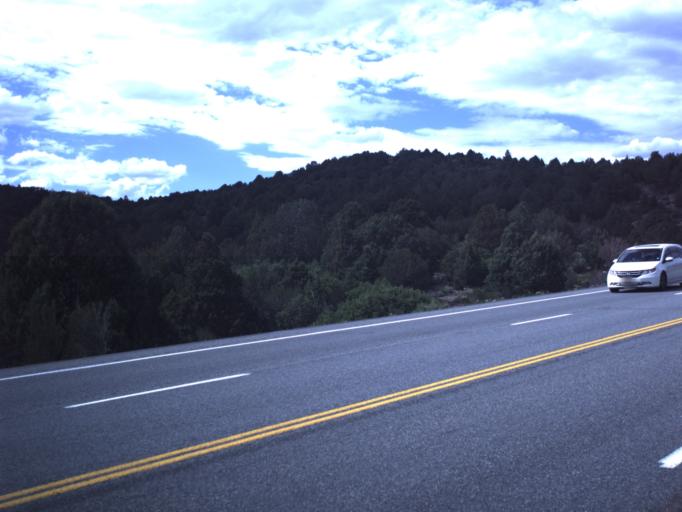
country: US
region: Utah
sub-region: Garfield County
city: Panguitch
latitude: 38.0243
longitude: -112.5318
